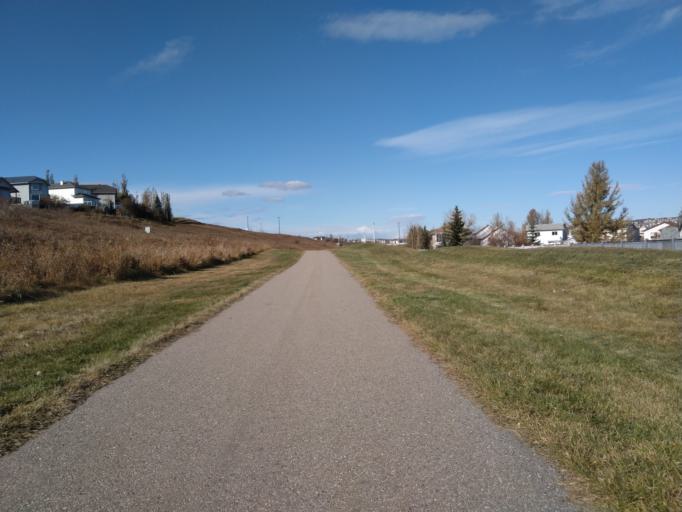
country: CA
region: Alberta
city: Calgary
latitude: 51.1523
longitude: -114.1146
